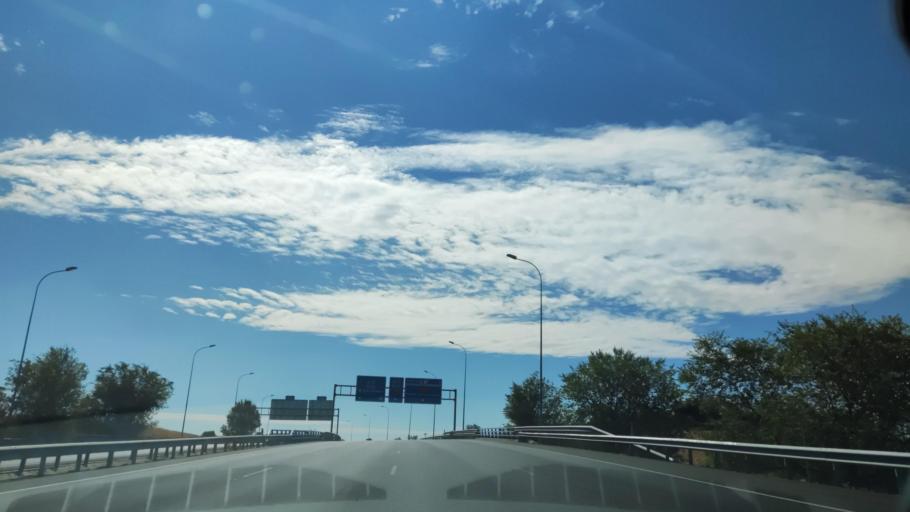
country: ES
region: Madrid
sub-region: Provincia de Madrid
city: Puente de Vallecas
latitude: 40.3698
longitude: -3.6507
